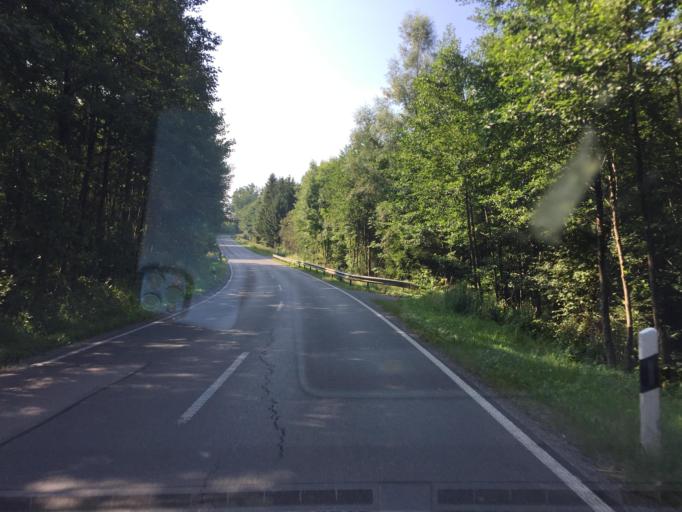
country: DE
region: Bavaria
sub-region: Upper Bavaria
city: Tuntenhausen
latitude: 47.9123
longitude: 11.9879
